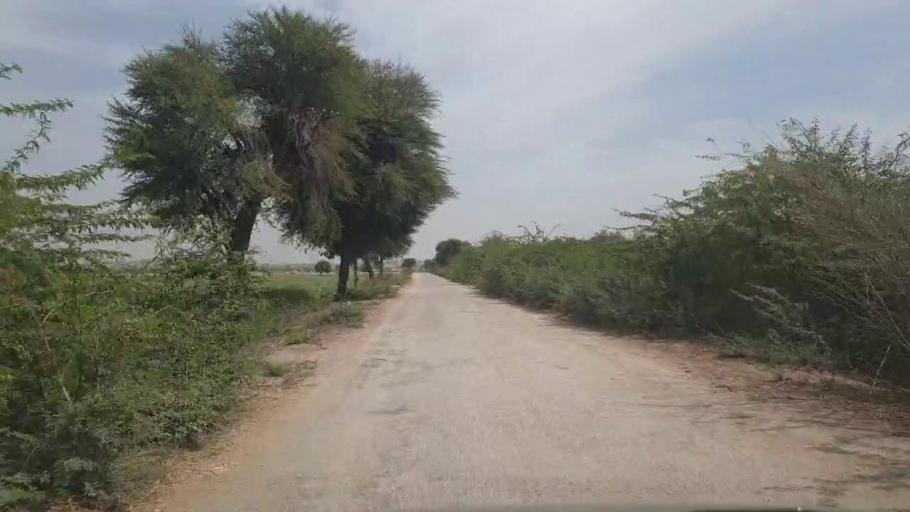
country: PK
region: Sindh
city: Umarkot
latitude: 25.2254
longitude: 69.7023
